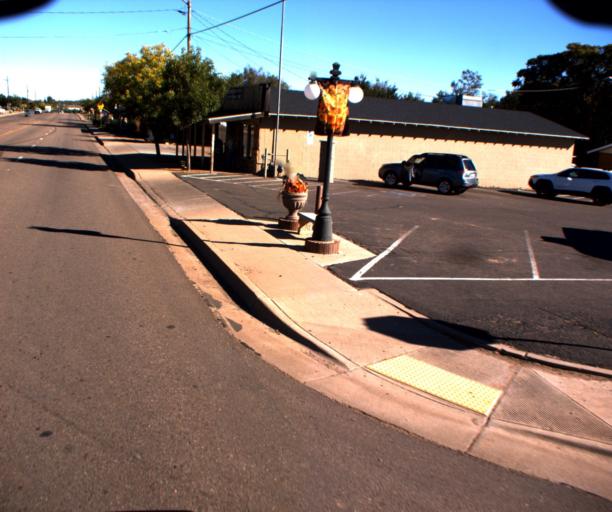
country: US
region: Arizona
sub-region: Navajo County
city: Taylor
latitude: 34.4637
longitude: -110.0911
